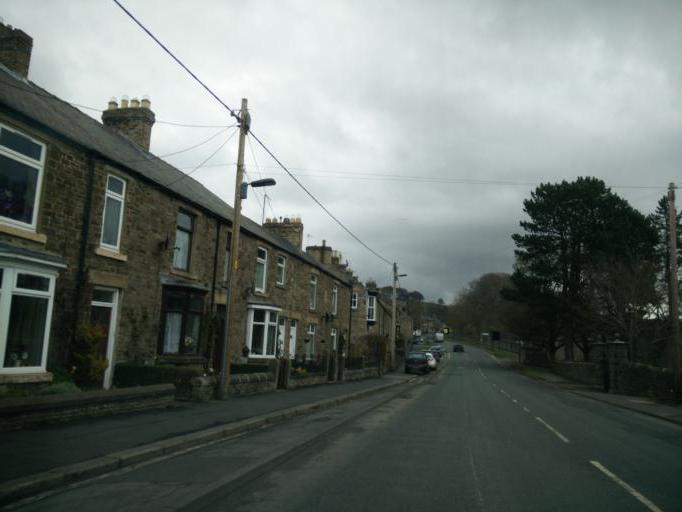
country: GB
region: England
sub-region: County Durham
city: Stanhope
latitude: 54.7488
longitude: -2.0160
